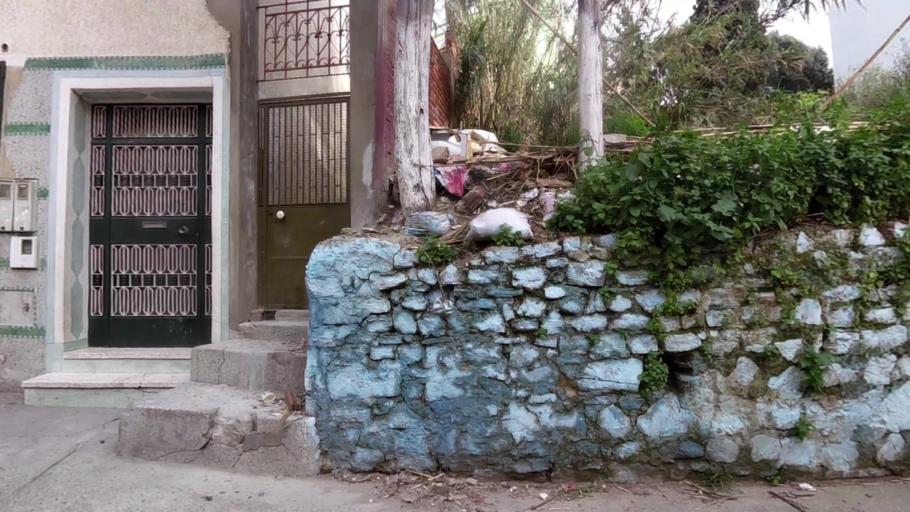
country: MA
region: Tanger-Tetouan
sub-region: Tanger-Assilah
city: Tangier
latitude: 35.7683
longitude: -5.7902
